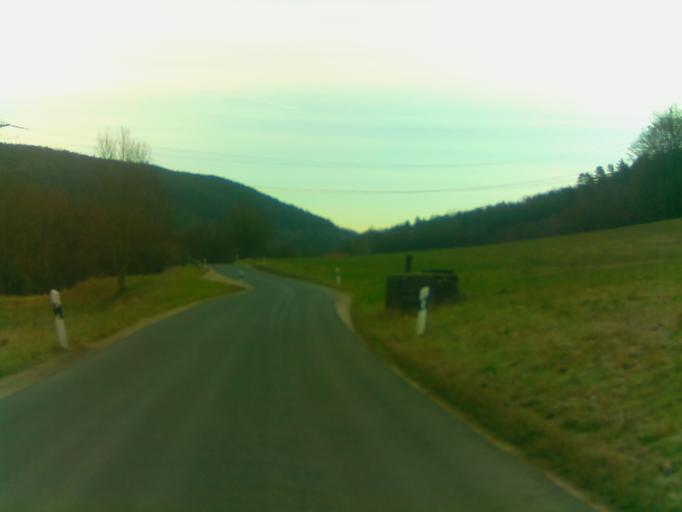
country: DE
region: Thuringia
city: Eichenberg
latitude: 50.7913
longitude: 11.5369
